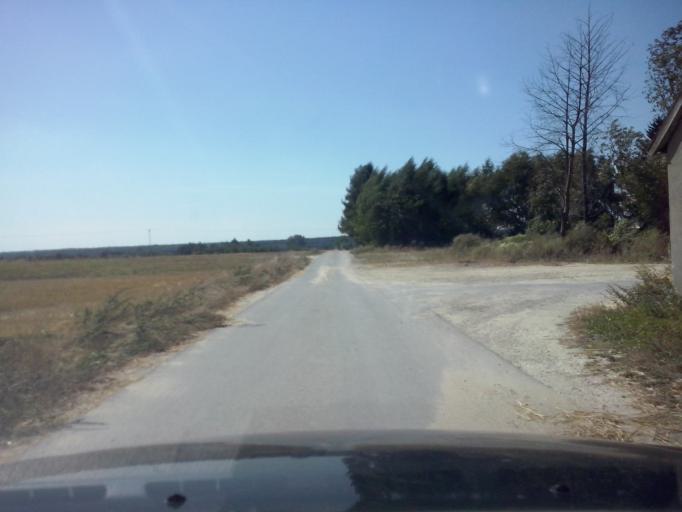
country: PL
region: Swietokrzyskie
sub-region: Powiat staszowski
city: Szydlow
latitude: 50.5851
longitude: 20.9318
